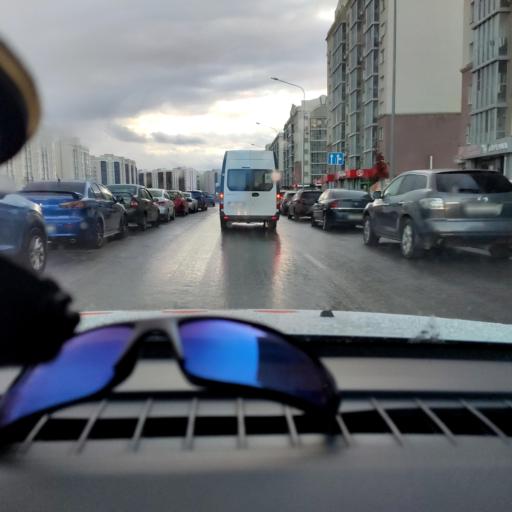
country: RU
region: Samara
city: Samara
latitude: 53.1138
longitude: 50.1476
